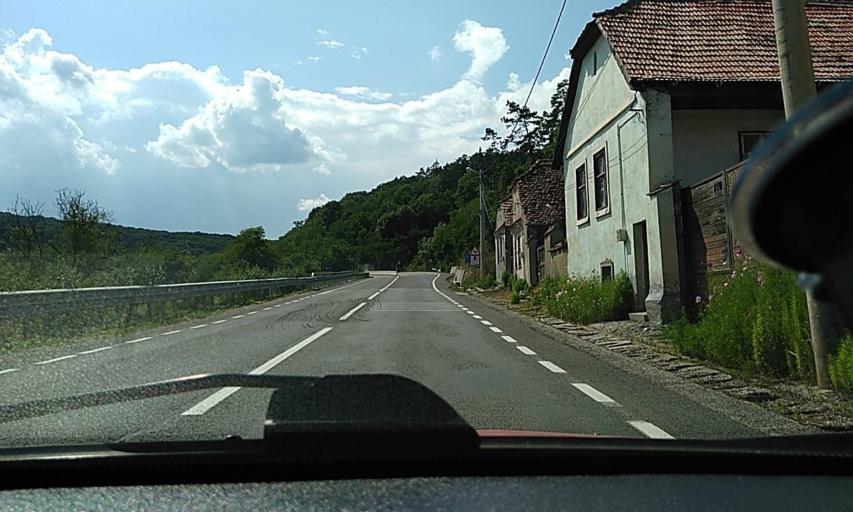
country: RO
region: Brasov
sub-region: Oras Rupea
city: Fiser
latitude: 46.0805
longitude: 25.1377
